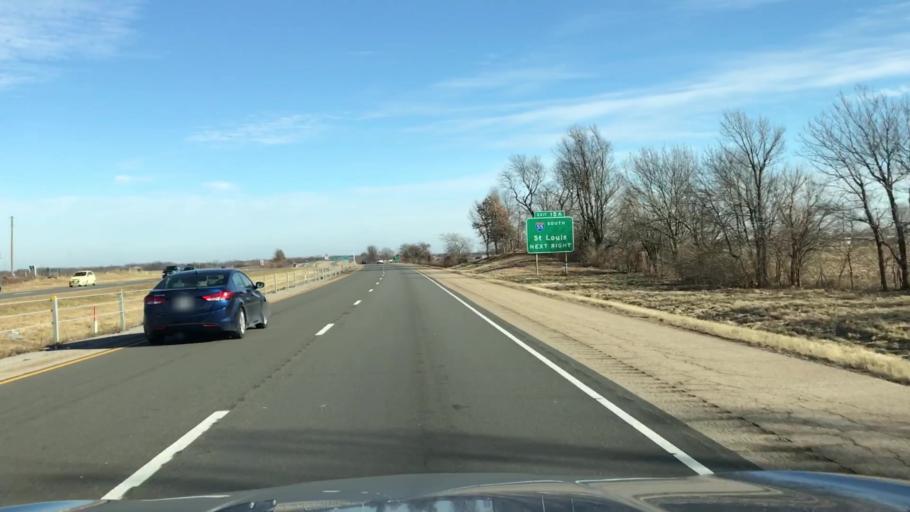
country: US
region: Illinois
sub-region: Madison County
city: Maryville
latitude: 38.7517
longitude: -89.9228
